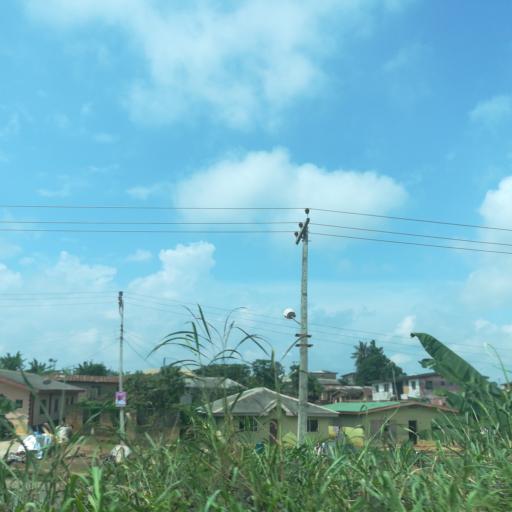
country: NG
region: Lagos
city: Ikorodu
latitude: 6.6649
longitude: 3.6760
